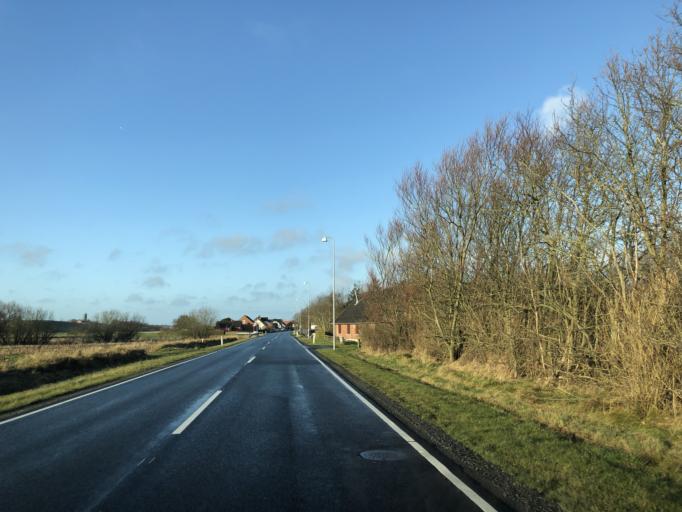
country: DK
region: Central Jutland
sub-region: Struer Kommune
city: Struer
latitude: 56.5476
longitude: 8.4918
